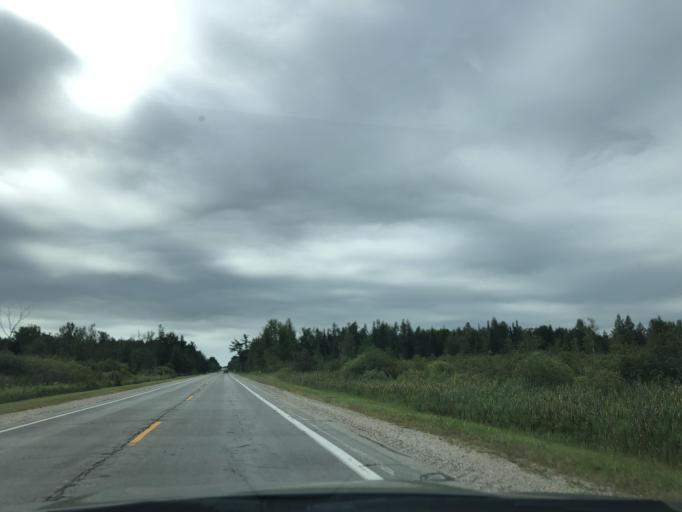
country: US
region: Michigan
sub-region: Missaukee County
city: Lake City
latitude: 44.2505
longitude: -85.2153
